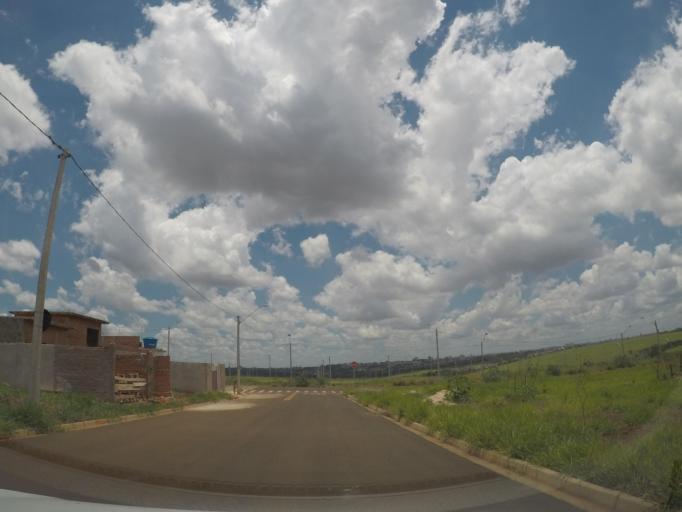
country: BR
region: Sao Paulo
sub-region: Hortolandia
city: Hortolandia
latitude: -22.8376
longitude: -47.2311
